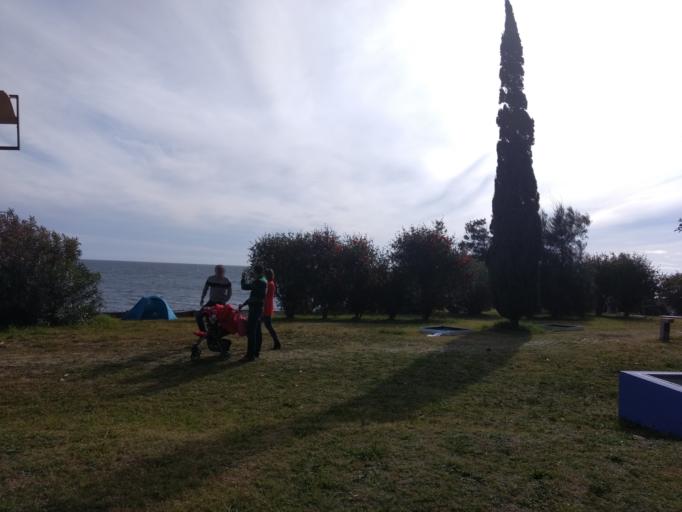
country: PT
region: Madeira
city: Calheta
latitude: 32.7171
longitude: -17.1697
